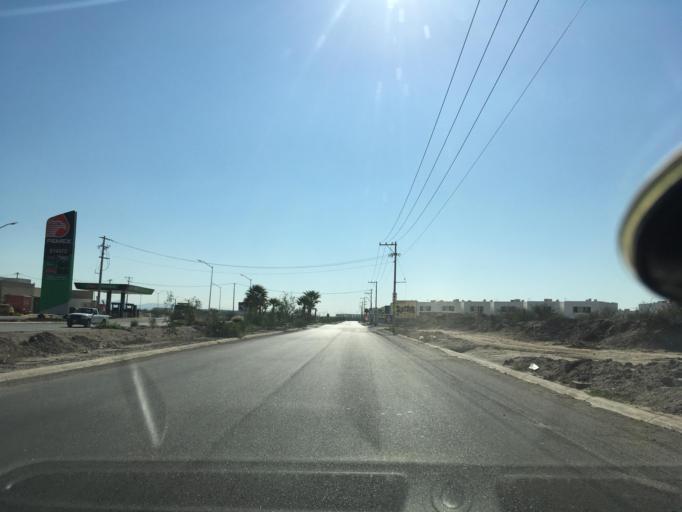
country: MX
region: Coahuila
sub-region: Torreon
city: Fraccionamiento la Noria
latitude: 25.5726
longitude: -103.3673
